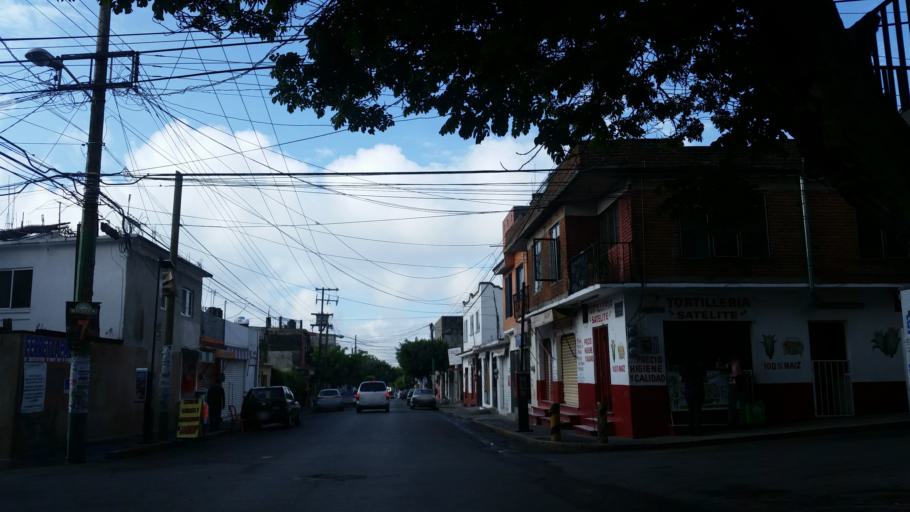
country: MX
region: Morelos
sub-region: Cuernavaca
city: Cuernavaca
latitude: 18.9184
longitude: -99.2067
